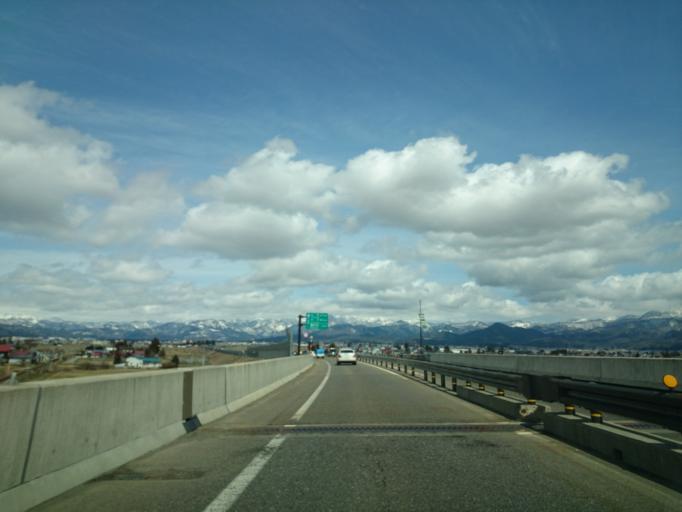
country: JP
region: Fukushima
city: Kitakata
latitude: 37.6128
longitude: 139.8825
